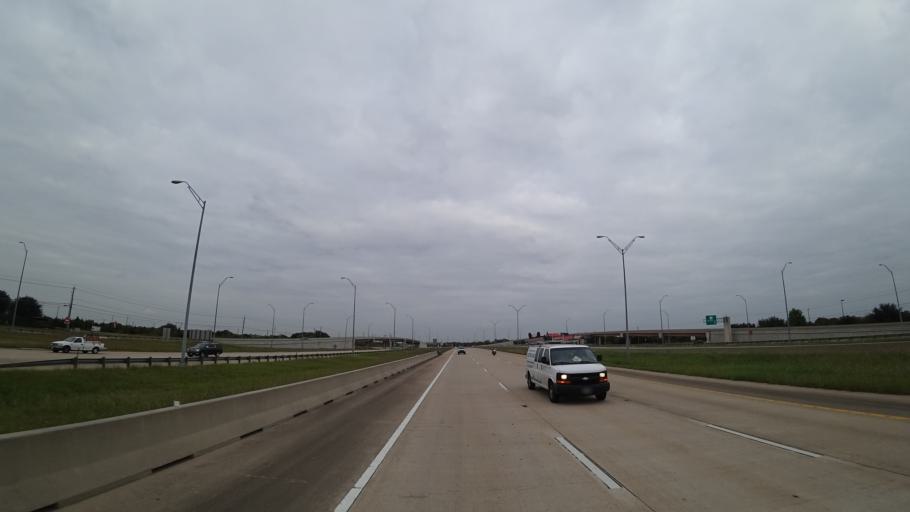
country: US
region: Texas
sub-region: Williamson County
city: Jollyville
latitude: 30.4747
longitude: -97.7740
